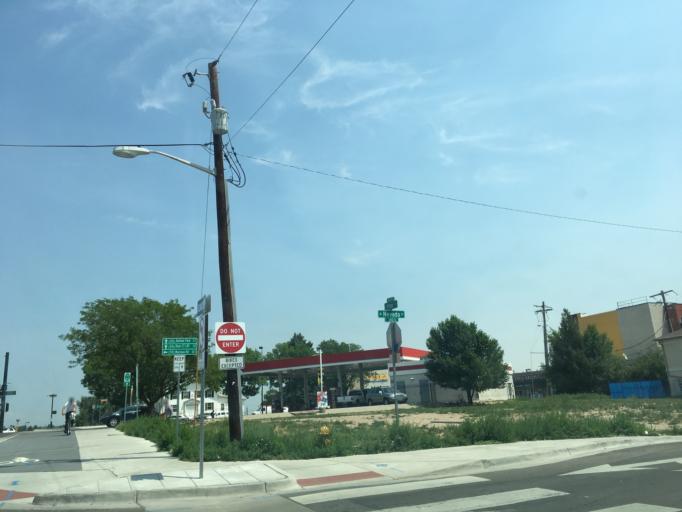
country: US
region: Colorado
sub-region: Jefferson County
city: Lakewood
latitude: 39.7102
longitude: -105.0325
